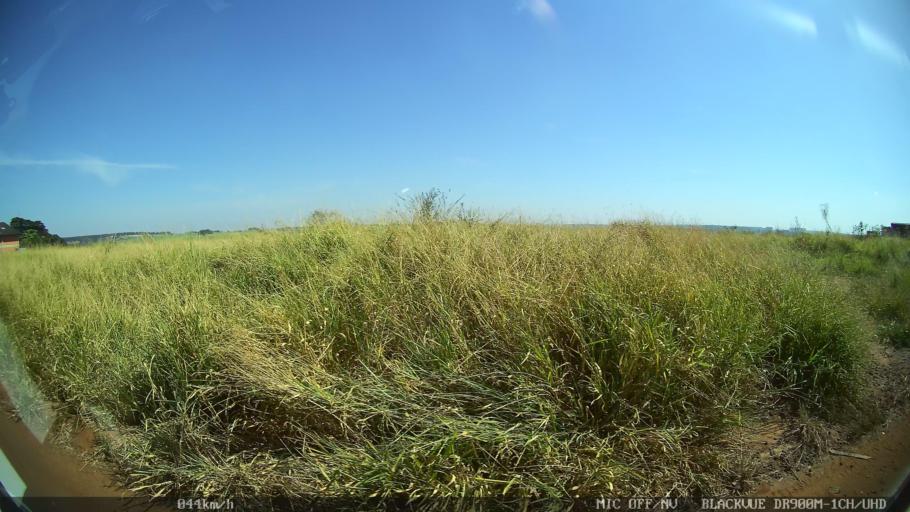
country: BR
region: Sao Paulo
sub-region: Batatais
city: Batatais
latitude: -20.8790
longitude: -47.6011
